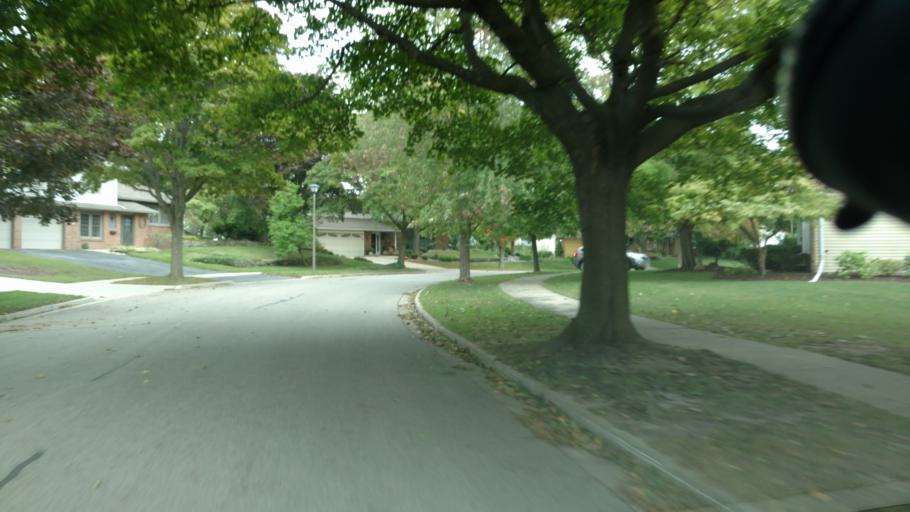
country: US
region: Michigan
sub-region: Ingham County
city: East Lansing
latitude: 42.7576
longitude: -84.5182
